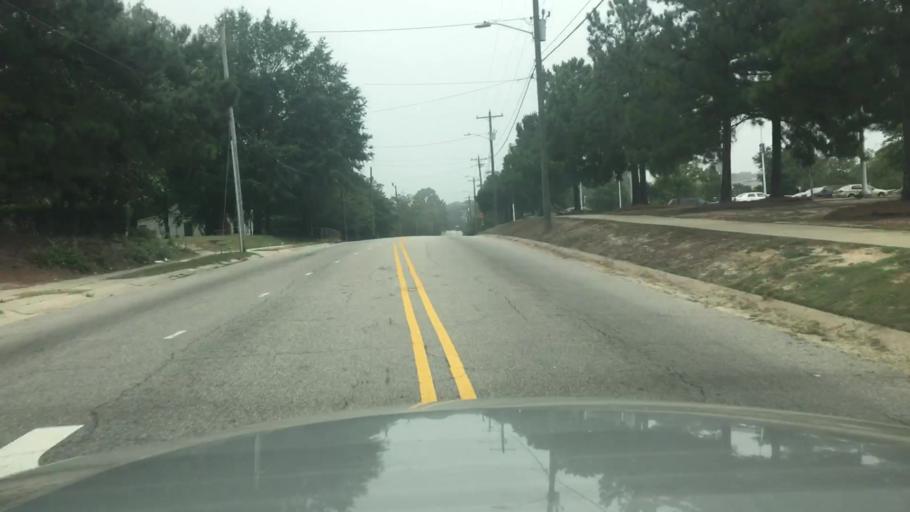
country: US
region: North Carolina
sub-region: Cumberland County
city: Fayetteville
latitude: 35.0710
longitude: -78.8837
